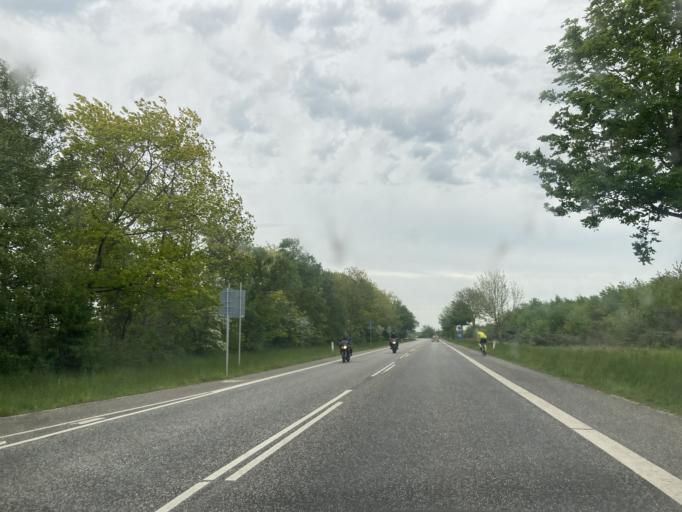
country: DK
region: Zealand
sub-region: Roskilde Kommune
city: Svogerslev
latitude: 55.6293
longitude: 12.0228
